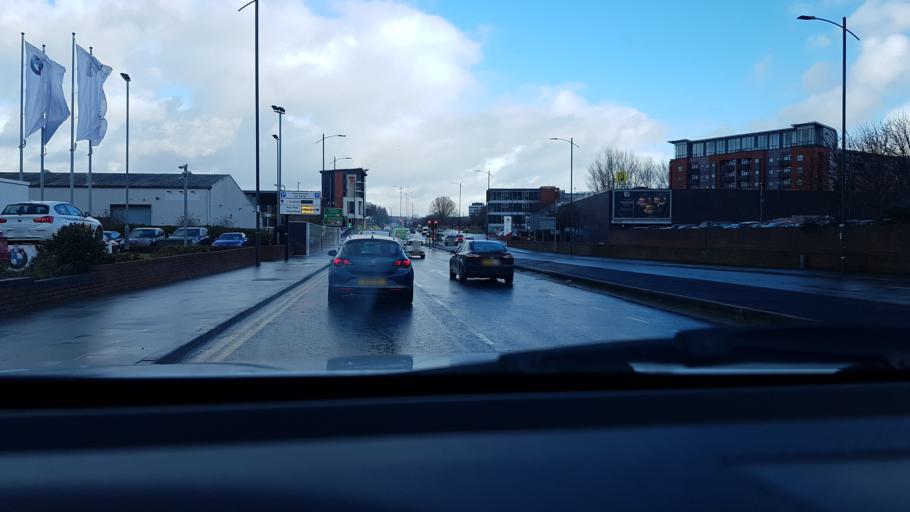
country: GB
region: England
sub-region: Liverpool
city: Liverpool
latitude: 53.4122
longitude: -2.9955
